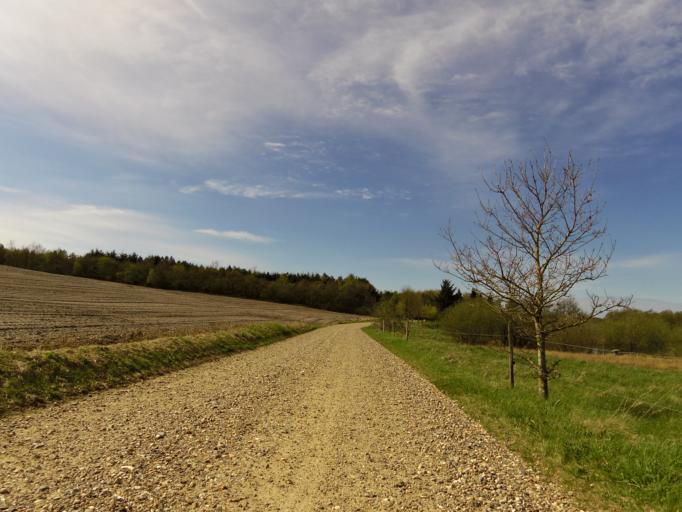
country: DK
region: Central Jutland
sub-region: Holstebro Kommune
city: Vinderup
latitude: 56.4680
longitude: 8.8877
